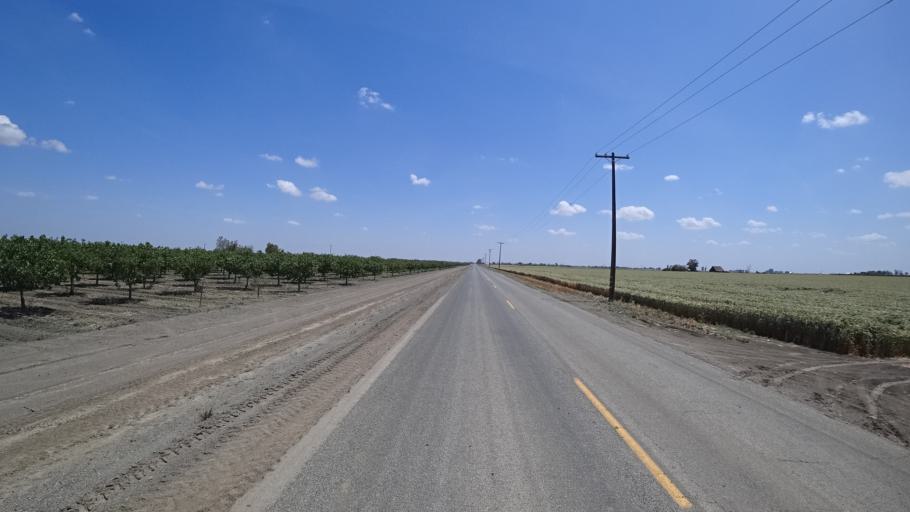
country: US
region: California
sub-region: Kings County
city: Stratford
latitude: 36.1895
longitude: -119.8594
